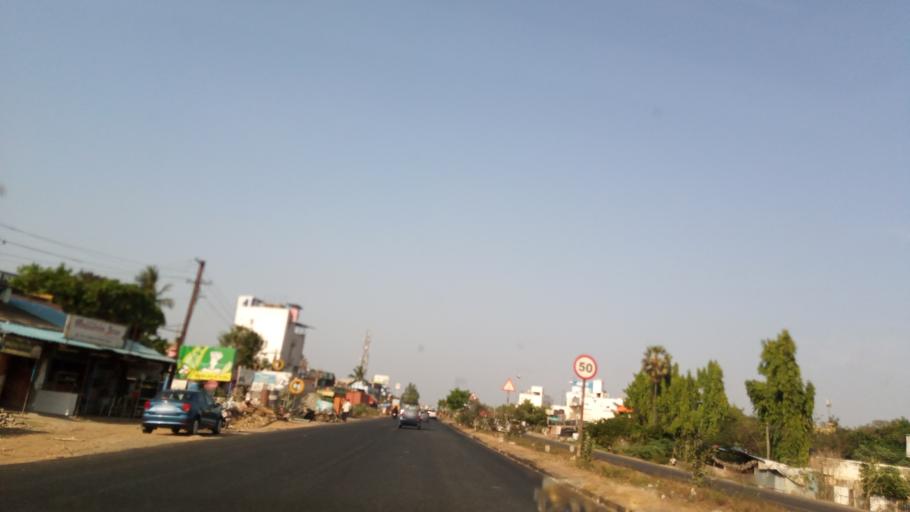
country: IN
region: Tamil Nadu
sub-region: Kancheepuram
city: Nandambakkam
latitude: 13.0318
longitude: 80.0358
